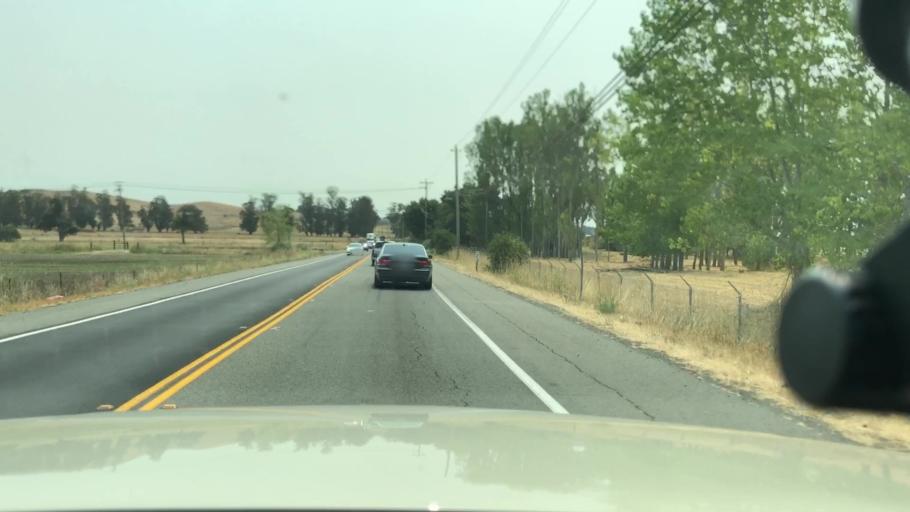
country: US
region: California
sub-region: Sonoma County
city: Petaluma
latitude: 38.2262
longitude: -122.5752
